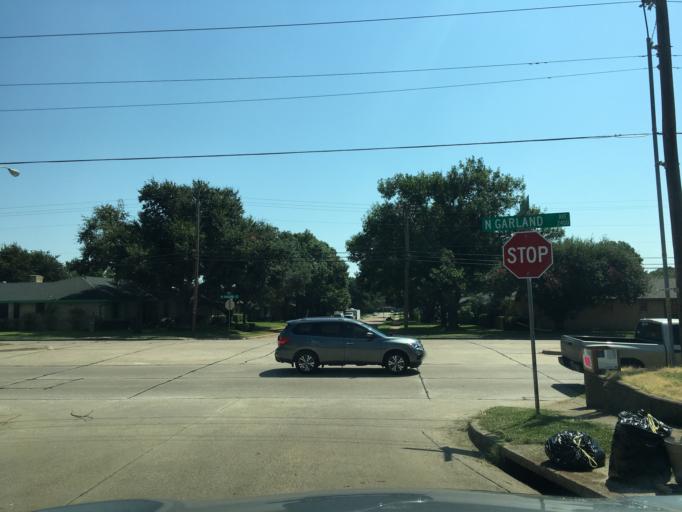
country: US
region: Texas
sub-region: Dallas County
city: Garland
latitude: 32.9373
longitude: -96.6486
